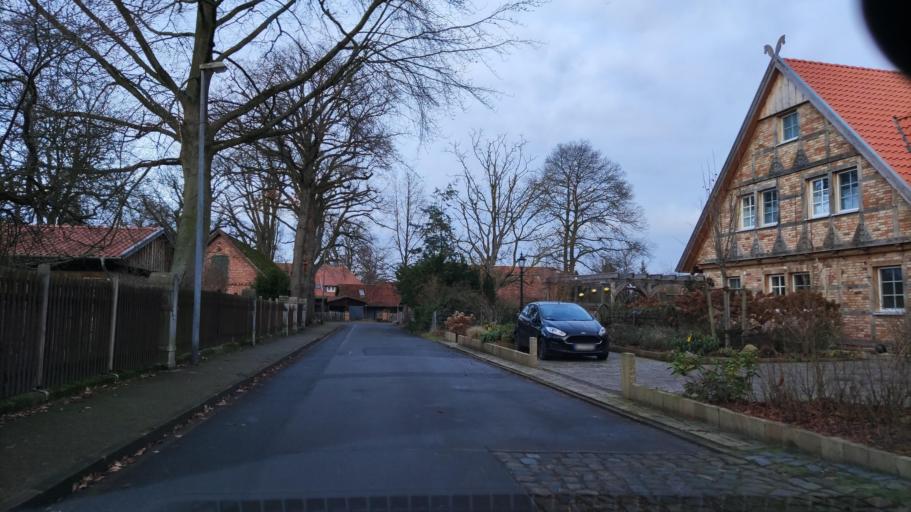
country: DE
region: Lower Saxony
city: Isernhagen Farster Bauerschaft
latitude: 52.5114
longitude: 9.9243
